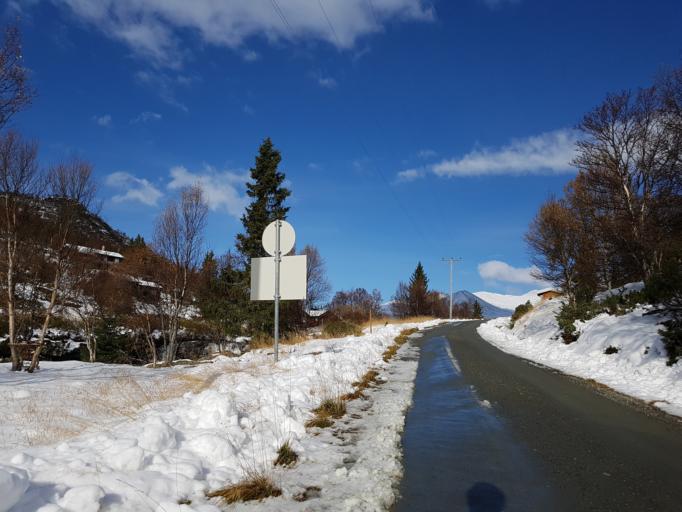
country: NO
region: Oppland
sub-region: Sel
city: Otta
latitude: 61.8184
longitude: 9.6775
